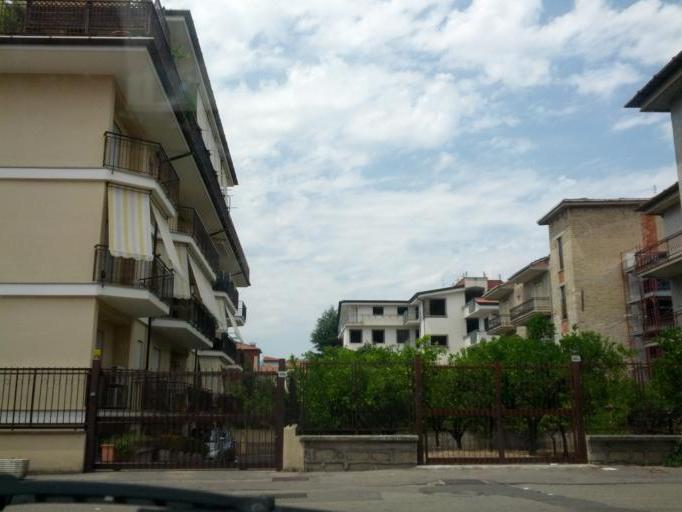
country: IT
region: Latium
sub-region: Provincia di Latina
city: Fondi
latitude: 41.3519
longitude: 13.4314
